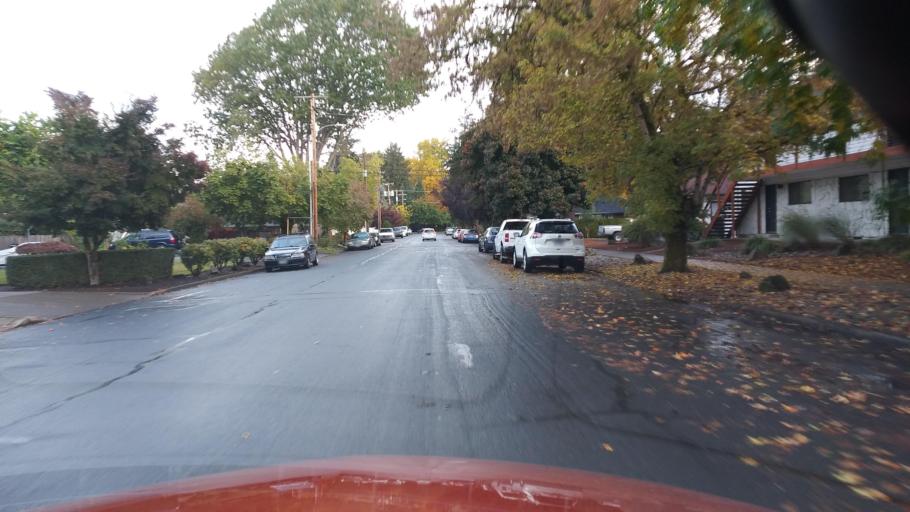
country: US
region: Oregon
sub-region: Washington County
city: Forest Grove
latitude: 45.5209
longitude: -123.1020
